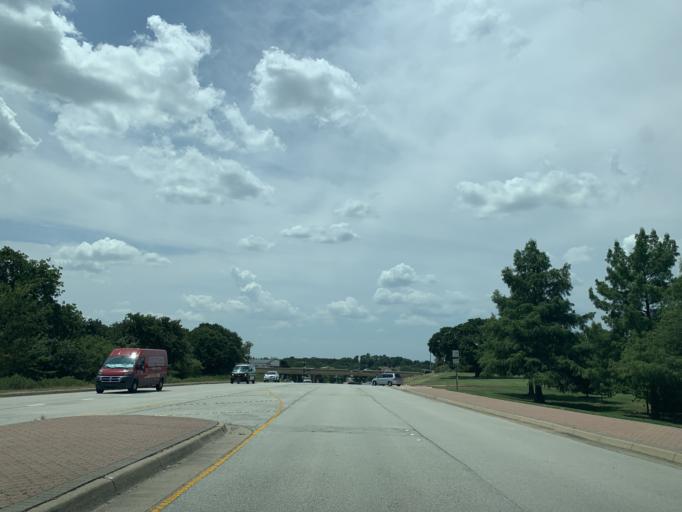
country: US
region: Texas
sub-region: Tarrant County
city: Southlake
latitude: 32.9704
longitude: -97.1556
